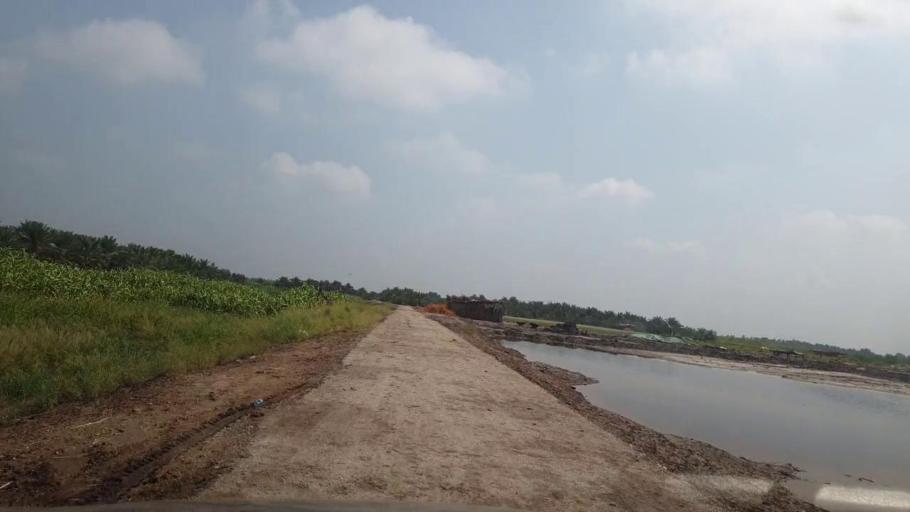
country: PK
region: Sindh
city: Pir jo Goth
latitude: 27.6000
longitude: 68.6935
